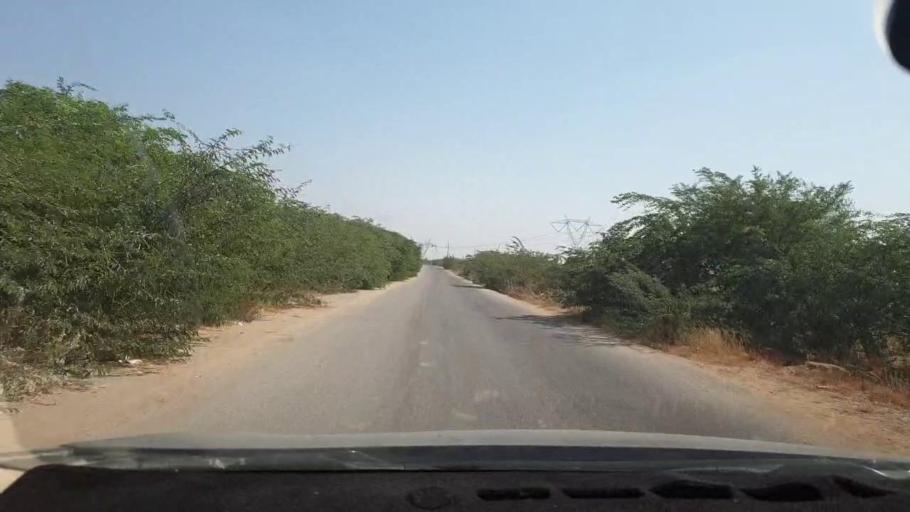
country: PK
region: Sindh
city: Malir Cantonment
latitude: 25.1446
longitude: 67.1879
